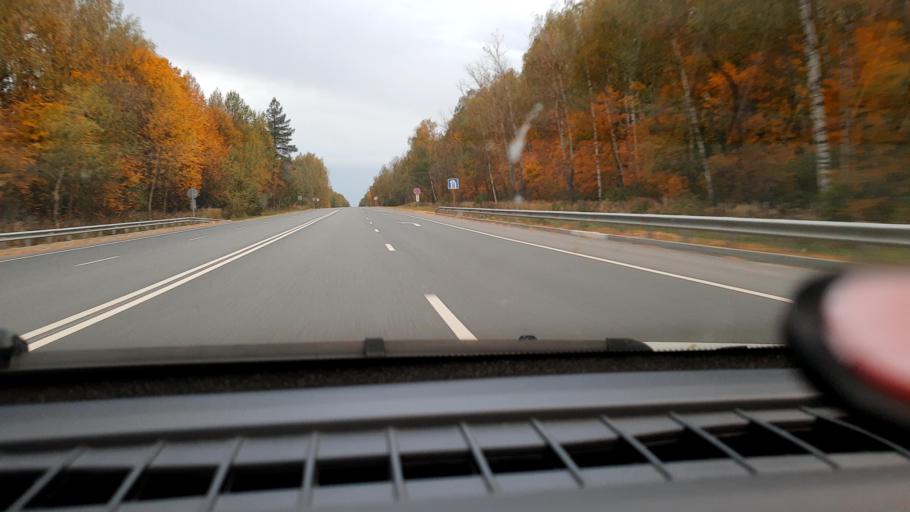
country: RU
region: Vladimir
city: Orgtrud
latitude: 56.2008
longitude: 40.7995
